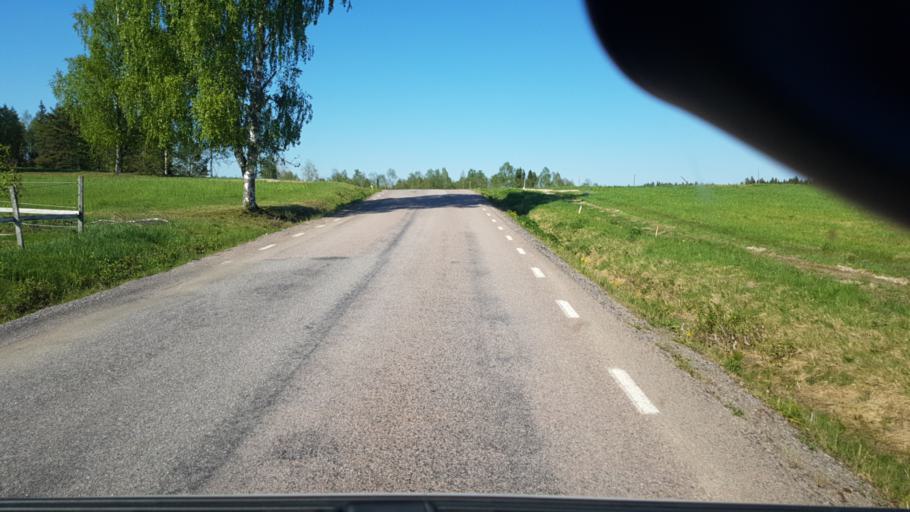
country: SE
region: Vaermland
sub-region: Eda Kommun
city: Charlottenberg
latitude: 59.8685
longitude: 12.3492
